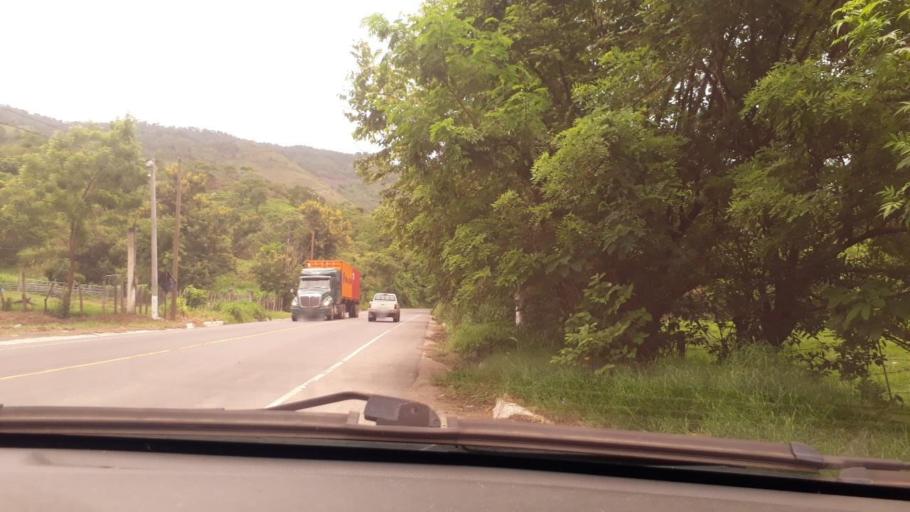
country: GT
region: Zacapa
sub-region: Municipio de Zacapa
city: Gualan
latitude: 15.1900
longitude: -89.2817
